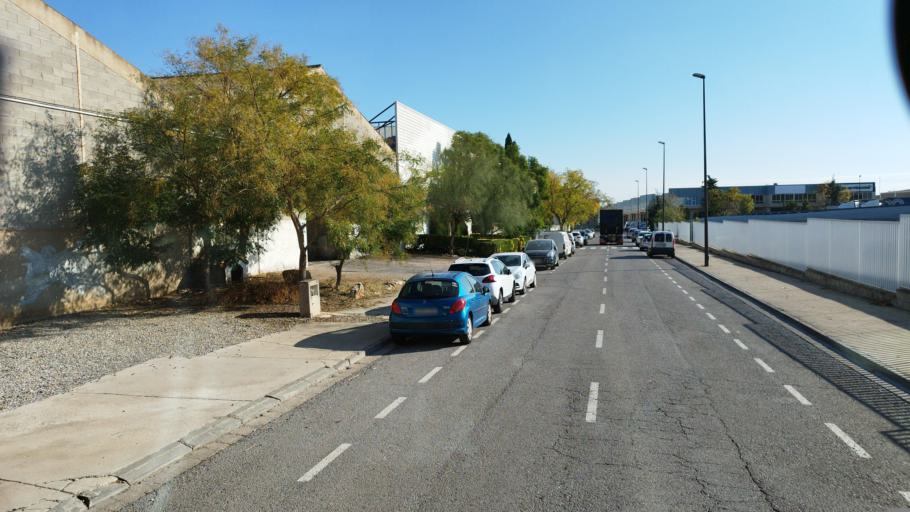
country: ES
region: Catalonia
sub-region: Provincia de Tarragona
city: Reus
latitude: 41.1578
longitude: 1.0763
